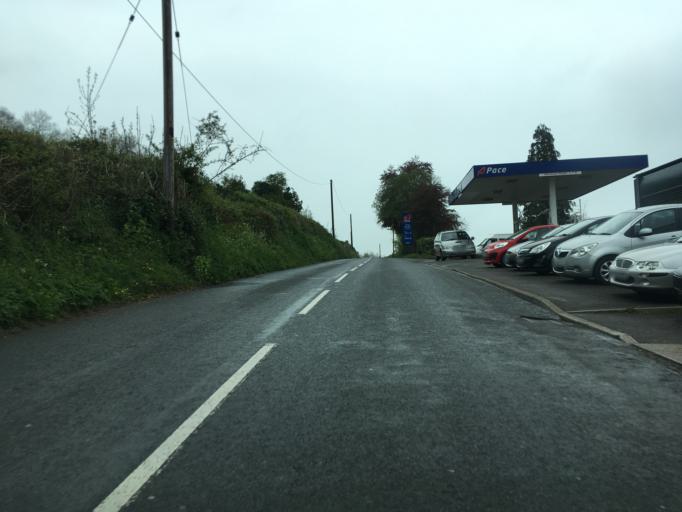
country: GB
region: England
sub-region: Bath and North East Somerset
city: Compton Martin
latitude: 51.3156
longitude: -2.6733
